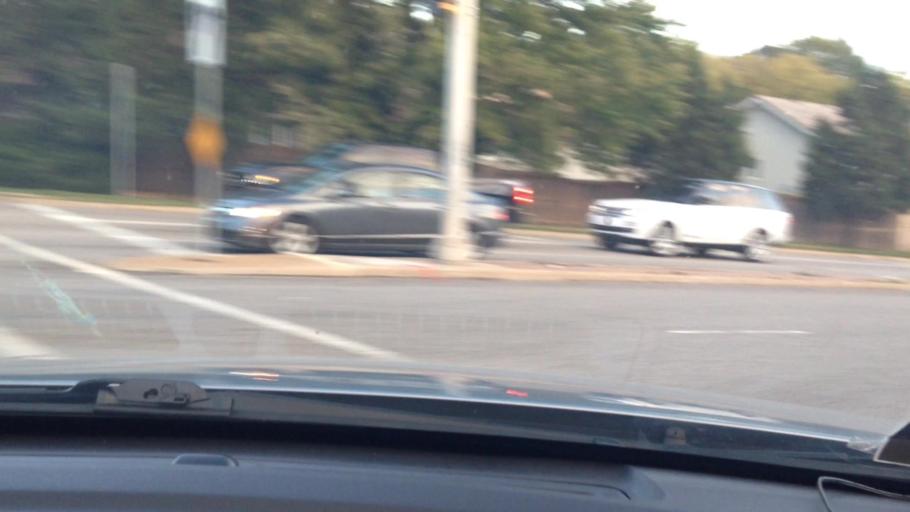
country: US
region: Kansas
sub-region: Johnson County
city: Leawood
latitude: 38.9421
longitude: -94.6398
